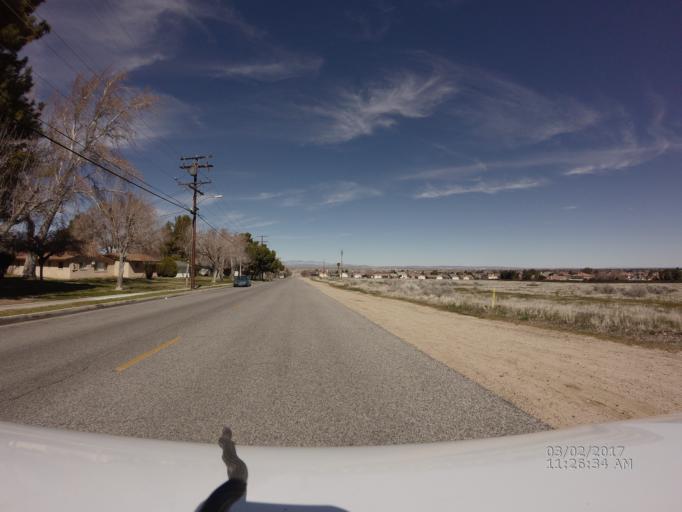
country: US
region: California
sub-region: Los Angeles County
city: Quartz Hill
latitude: 34.6464
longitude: -118.2449
